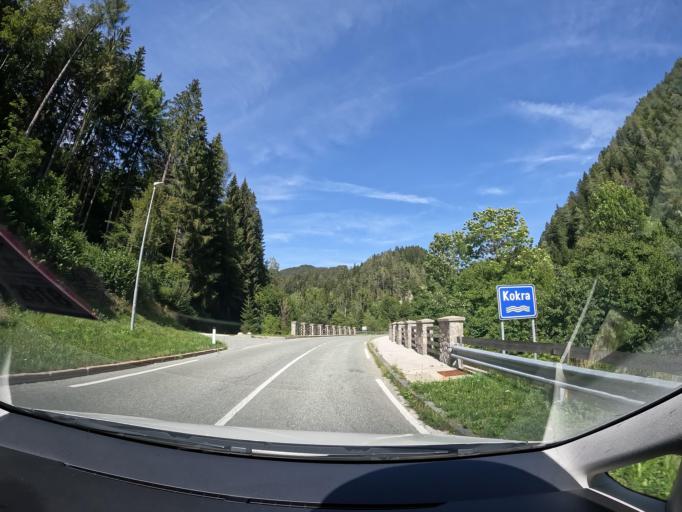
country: SI
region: Jesenice
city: Slovenski Javornik
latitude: 46.4202
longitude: 14.0961
